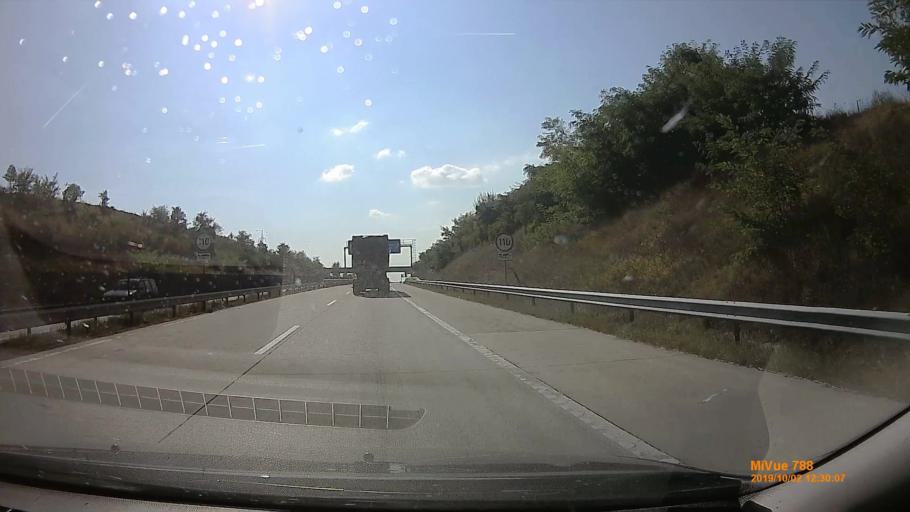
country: HU
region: Pest
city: Nagytarcsa
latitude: 47.5227
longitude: 19.3033
